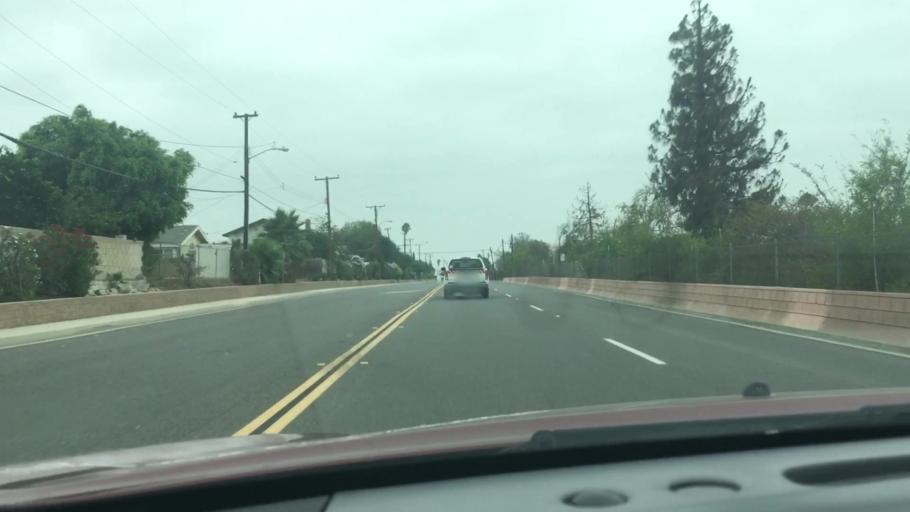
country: US
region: California
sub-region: Orange County
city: Buena Park
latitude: 33.8858
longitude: -118.0078
